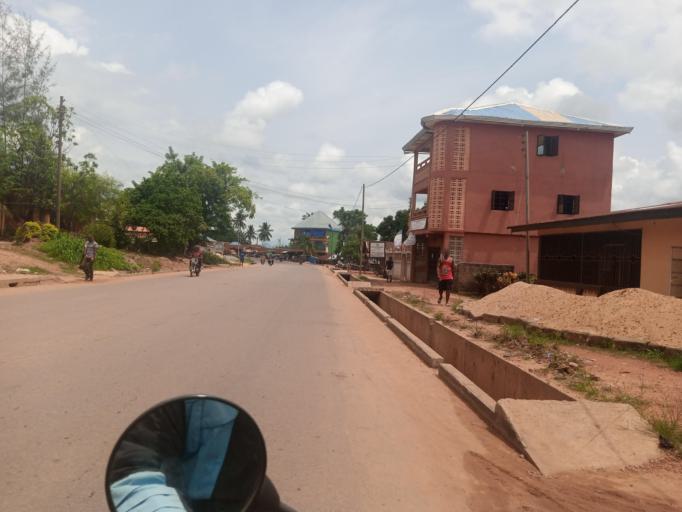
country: SL
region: Southern Province
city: Bo
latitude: 7.9523
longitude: -11.7529
